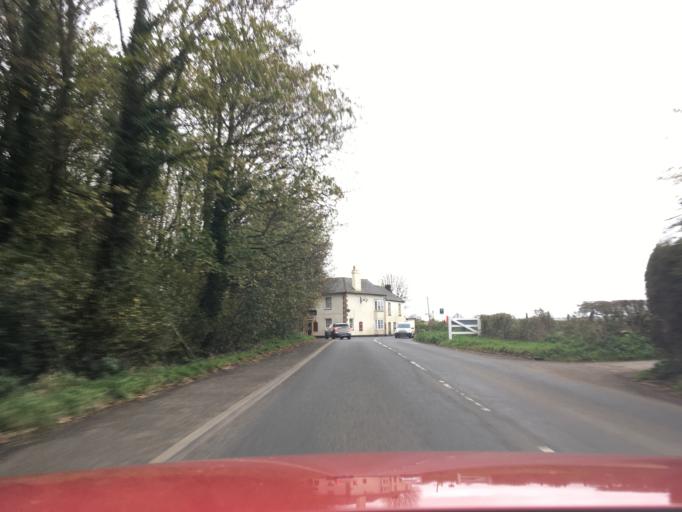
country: GB
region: England
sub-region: Somerset
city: Yeovil
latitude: 50.9972
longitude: -2.5838
